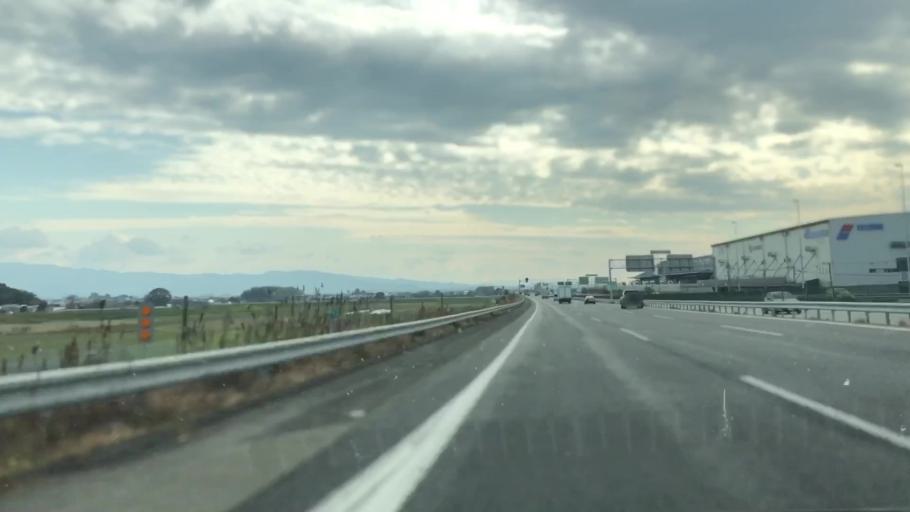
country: JP
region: Saga Prefecture
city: Tosu
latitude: 33.3918
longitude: 130.5384
